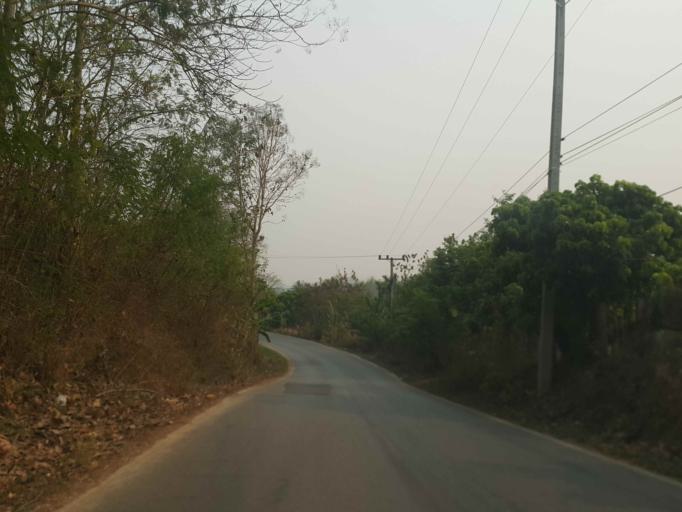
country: TH
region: Chiang Mai
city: Mae Taeng
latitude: 19.0991
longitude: 98.9001
